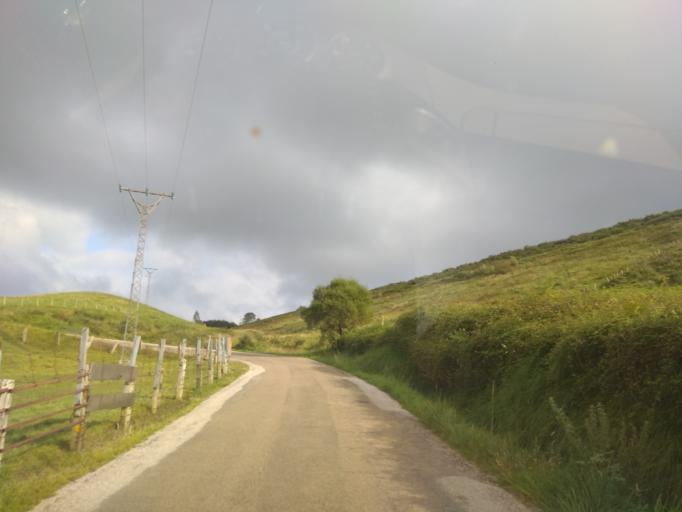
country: ES
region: Cantabria
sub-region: Provincia de Cantabria
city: San Vicente de la Barquera
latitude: 43.3132
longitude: -4.3850
